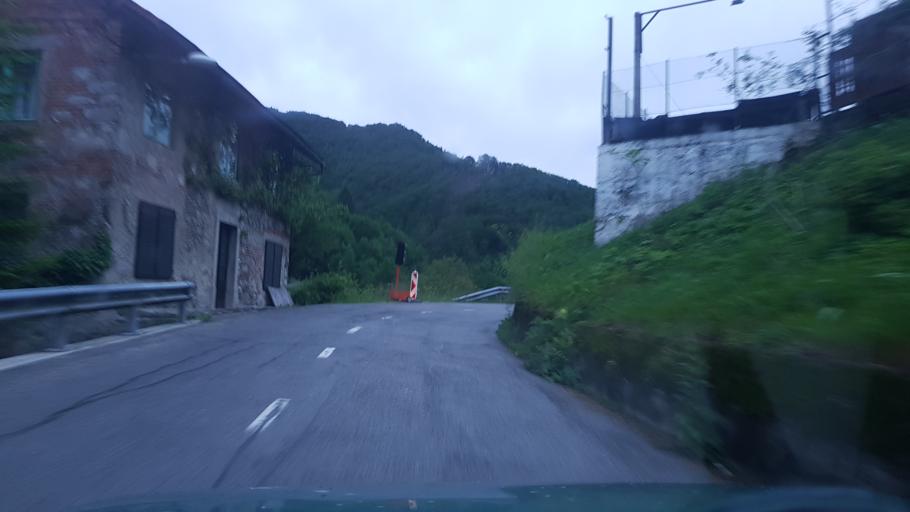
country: SI
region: Cerkno
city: Cerkno
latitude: 46.1744
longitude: 13.9143
